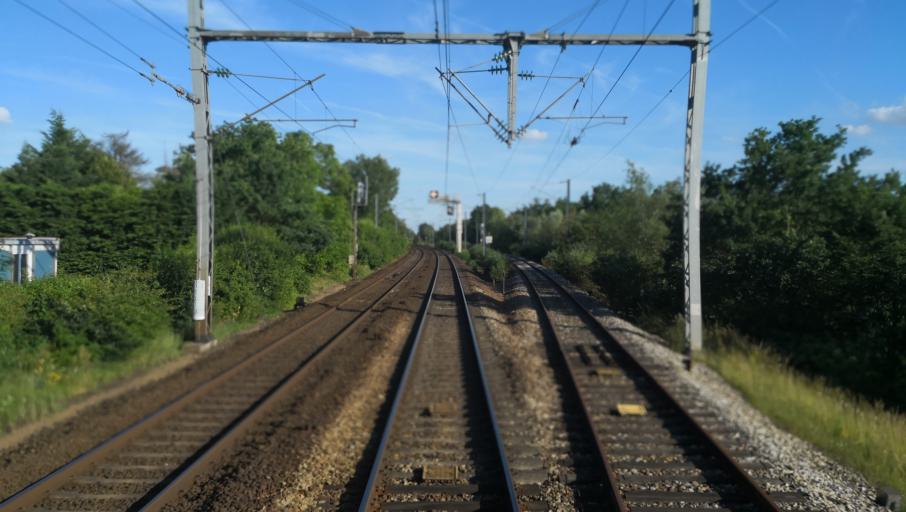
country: FR
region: Haute-Normandie
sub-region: Departement de l'Eure
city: Bueil
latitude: 48.9291
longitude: 1.4398
